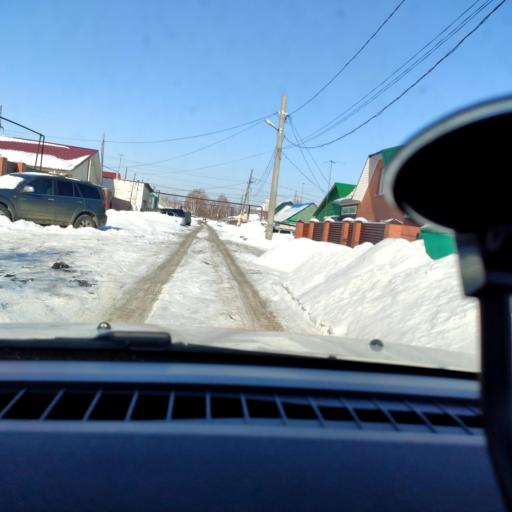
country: RU
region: Samara
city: Samara
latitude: 53.1315
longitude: 50.1303
